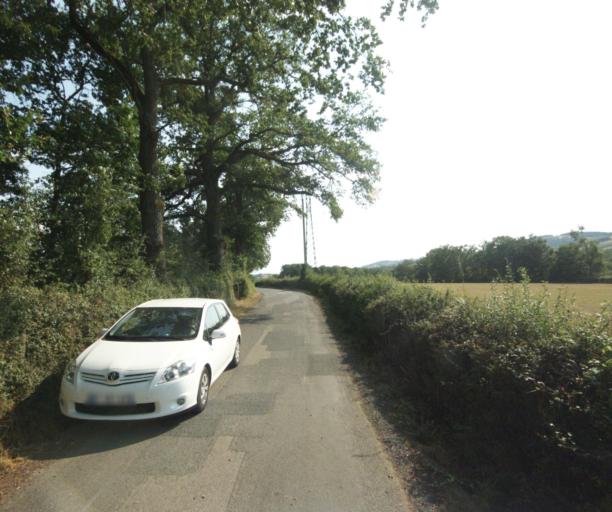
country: FR
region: Rhone-Alpes
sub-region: Departement du Rhone
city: Savigny
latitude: 45.8323
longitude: 4.5864
